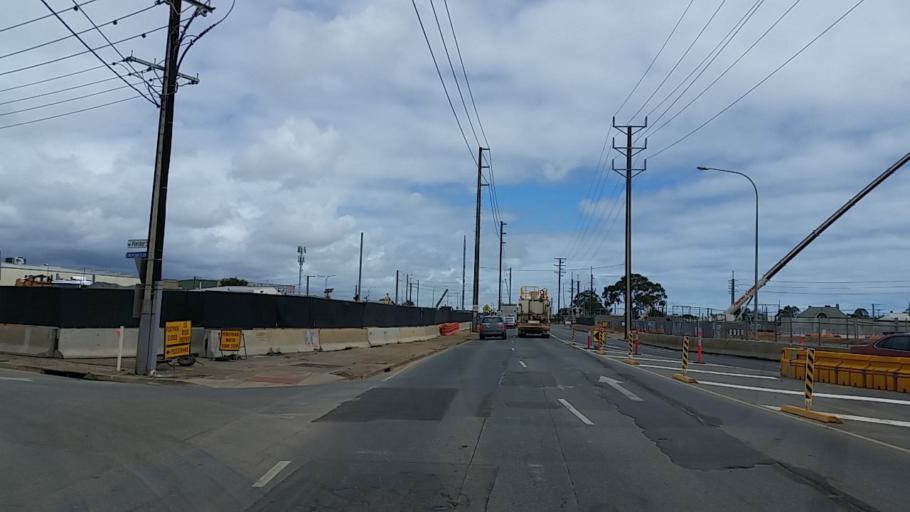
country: AU
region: South Australia
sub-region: Charles Sturt
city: Allenby Gardens
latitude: -34.8978
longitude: 138.5674
